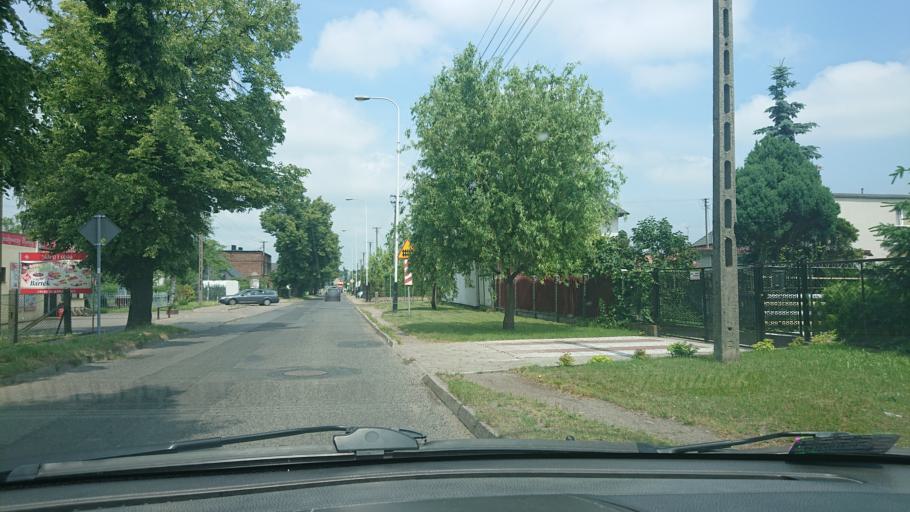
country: PL
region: Greater Poland Voivodeship
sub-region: Powiat gnieznienski
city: Gniezno
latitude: 52.5235
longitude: 17.5816
